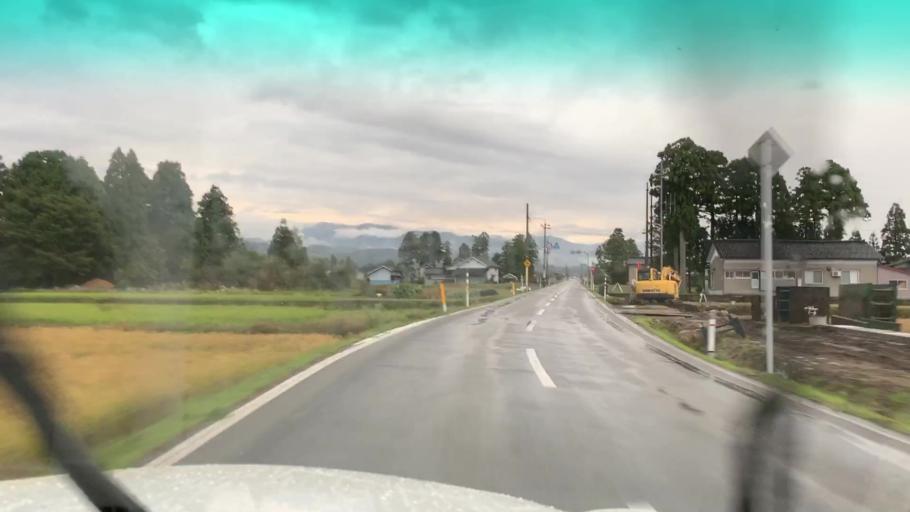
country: JP
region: Toyama
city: Kamiichi
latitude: 36.6453
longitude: 137.3285
